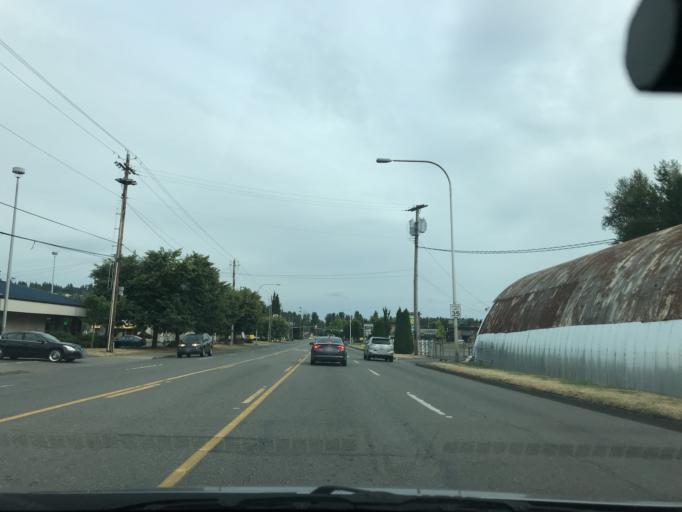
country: US
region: Washington
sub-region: King County
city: Pacific
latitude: 47.2746
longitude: -122.2289
